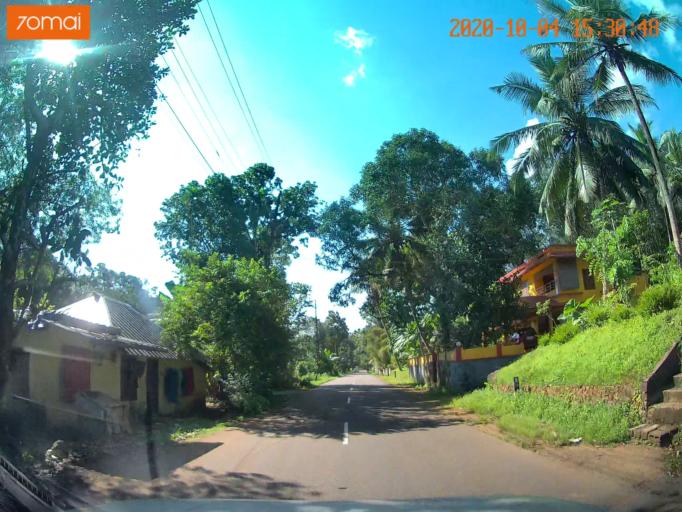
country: IN
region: Kerala
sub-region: Kottayam
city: Palackattumala
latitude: 9.7258
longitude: 76.6419
